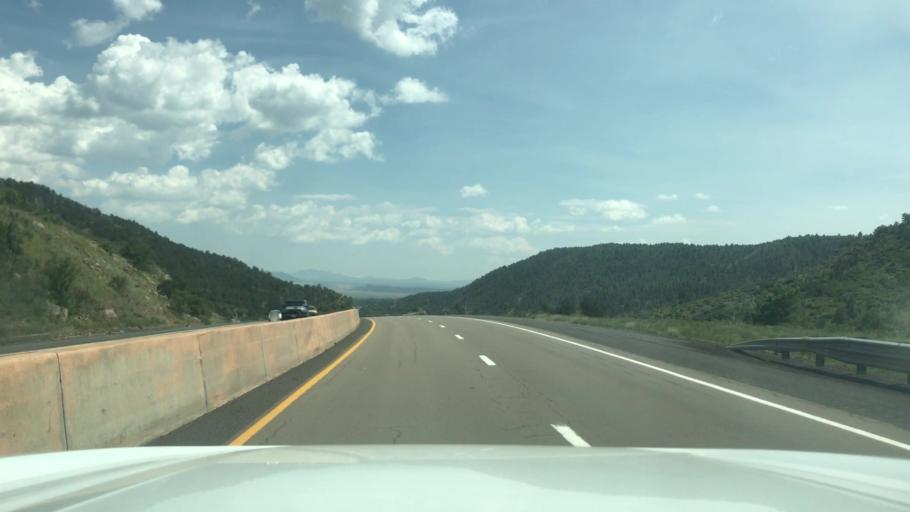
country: US
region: New Mexico
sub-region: Colfax County
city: Raton
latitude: 36.9288
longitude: -104.4566
